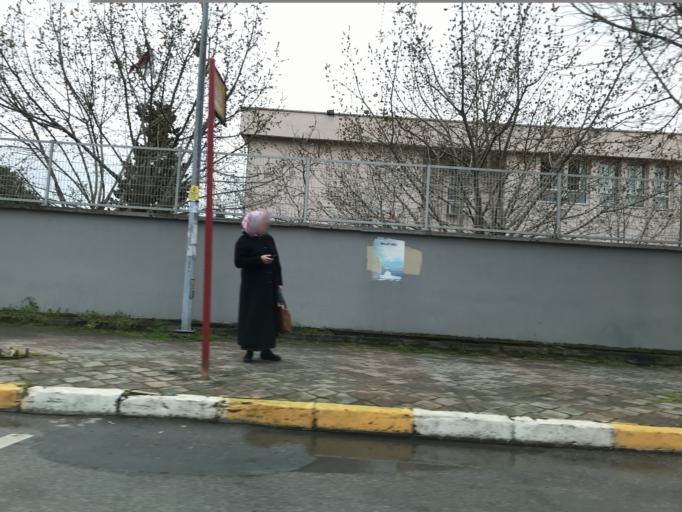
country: TR
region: Istanbul
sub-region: Atasehir
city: Atasehir
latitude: 40.9864
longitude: 29.0961
